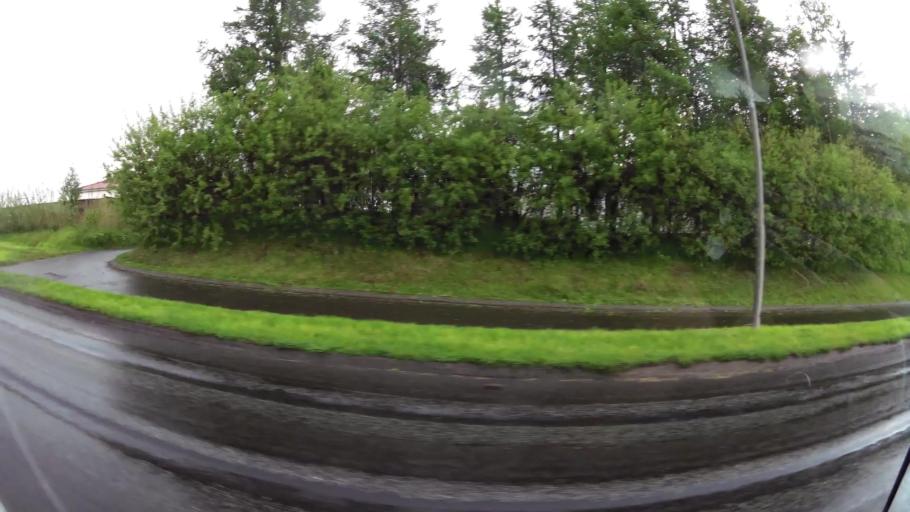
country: IS
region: Northeast
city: Akureyri
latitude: 65.6873
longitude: -18.1303
